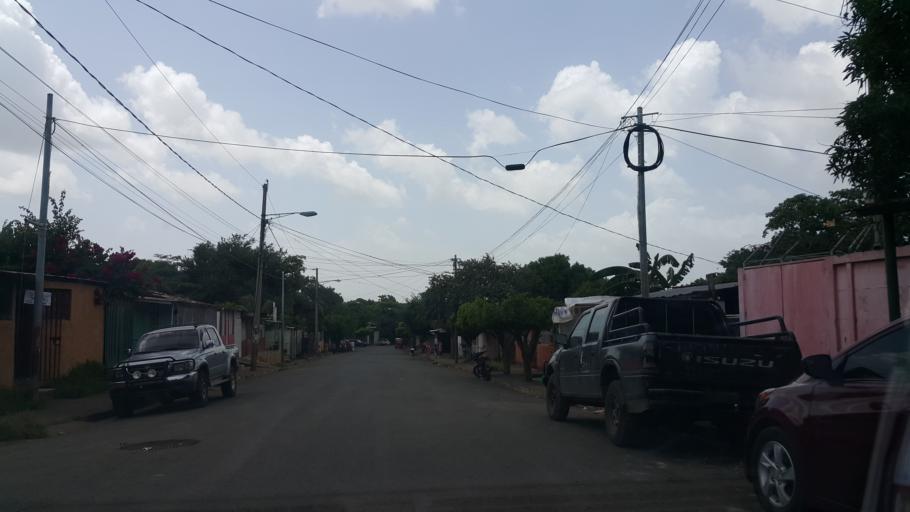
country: NI
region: Managua
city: Managua
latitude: 12.1170
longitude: -86.2422
